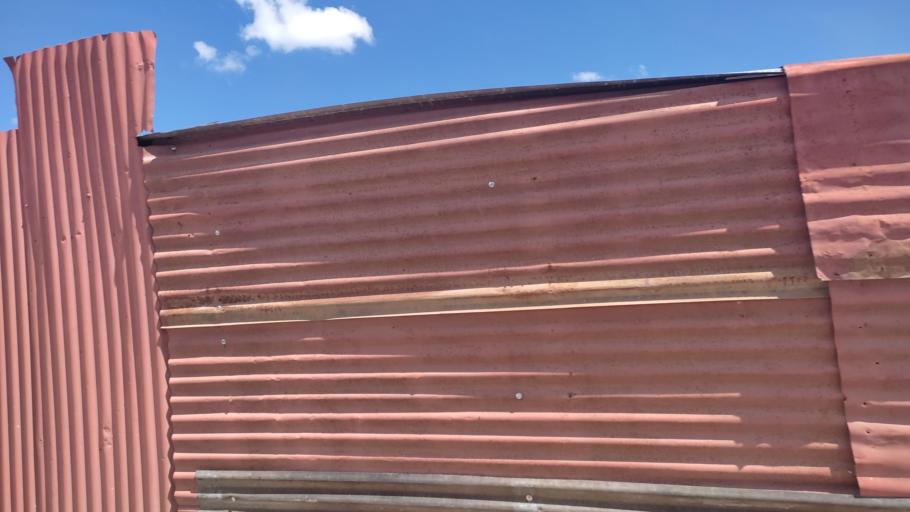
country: GT
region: Quetzaltenango
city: Quetzaltenango
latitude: 14.8561
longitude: -91.5274
